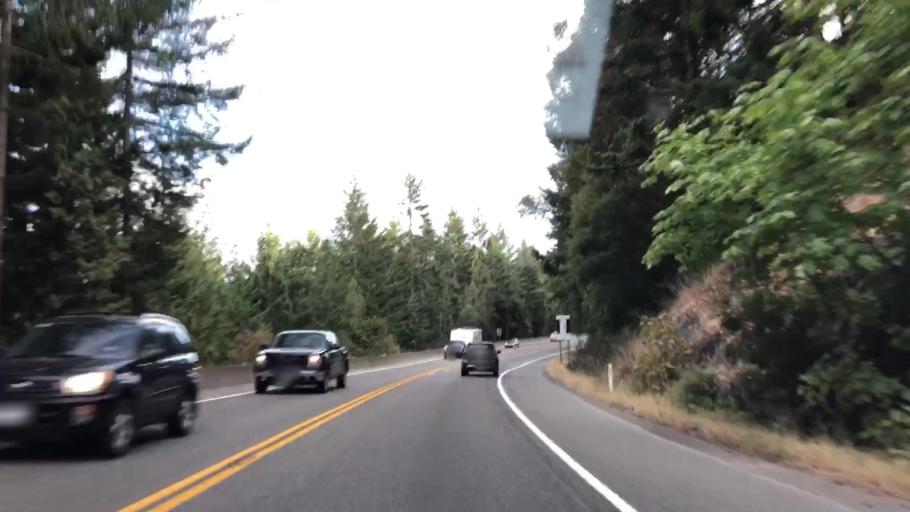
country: CA
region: British Columbia
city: Langford
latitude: 48.5760
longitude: -123.5271
